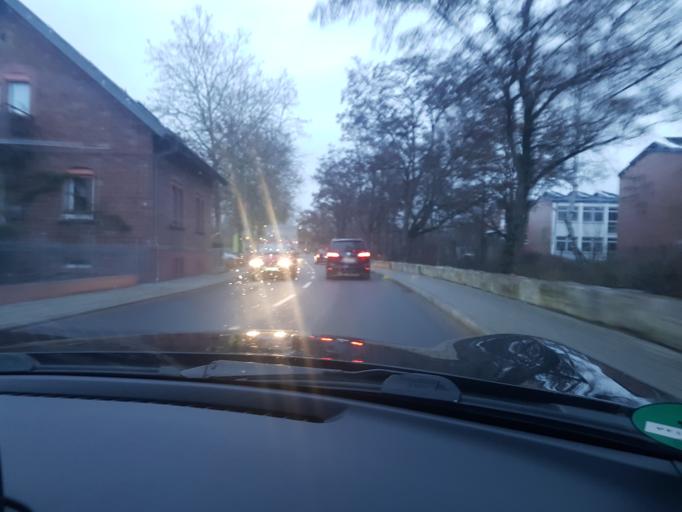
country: DE
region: Baden-Wuerttemberg
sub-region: Karlsruhe Region
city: Buchen
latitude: 49.5203
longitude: 9.3251
